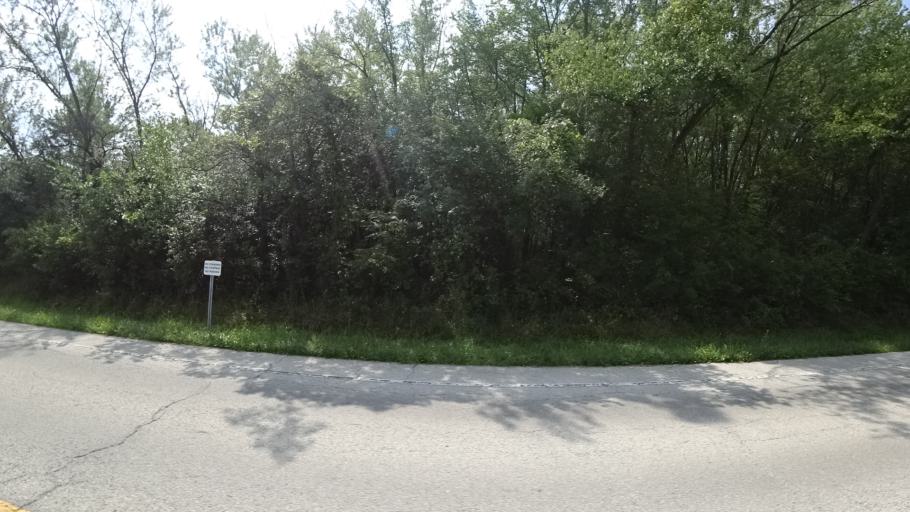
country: US
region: Illinois
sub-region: Will County
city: Goodings Grove
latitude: 41.6565
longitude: -87.9123
